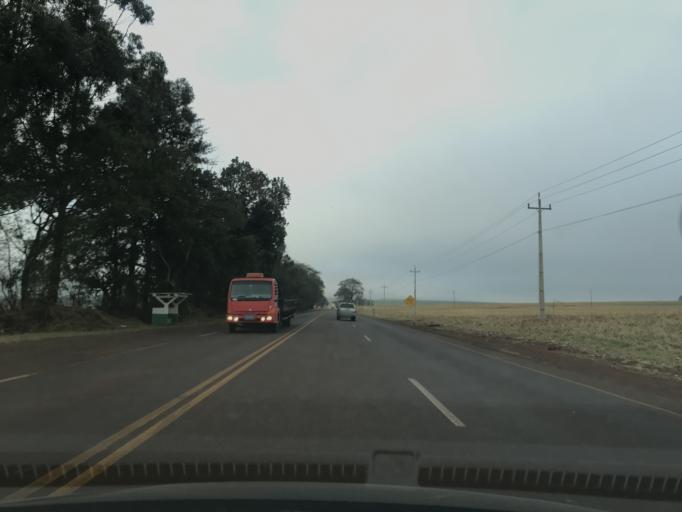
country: BR
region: Parana
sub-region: Toledo
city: Toledo
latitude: -24.6452
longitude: -53.7080
